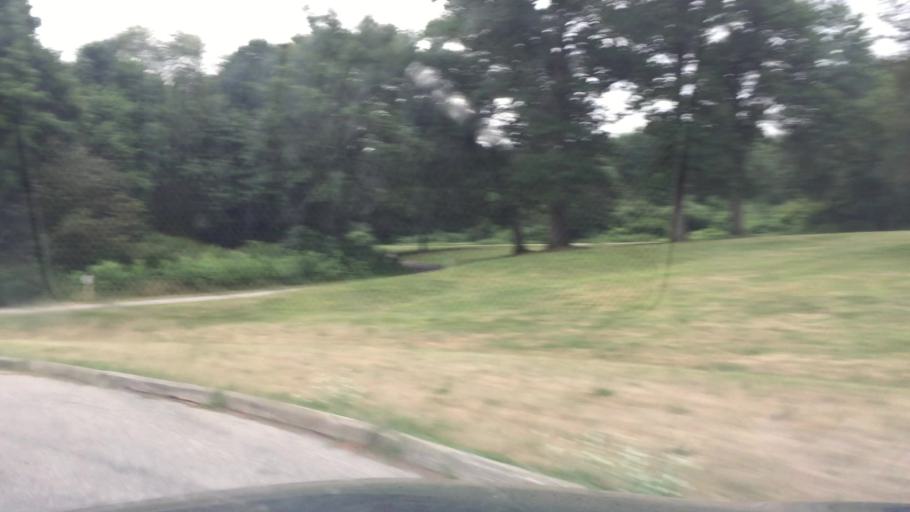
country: US
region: Michigan
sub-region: Oakland County
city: South Lyon
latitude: 42.5107
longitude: -83.6745
